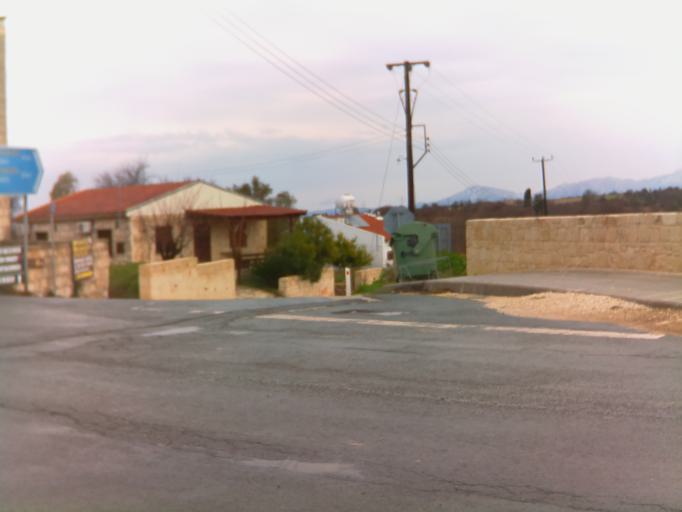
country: CY
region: Pafos
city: Pegeia
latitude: 34.9134
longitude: 32.4260
